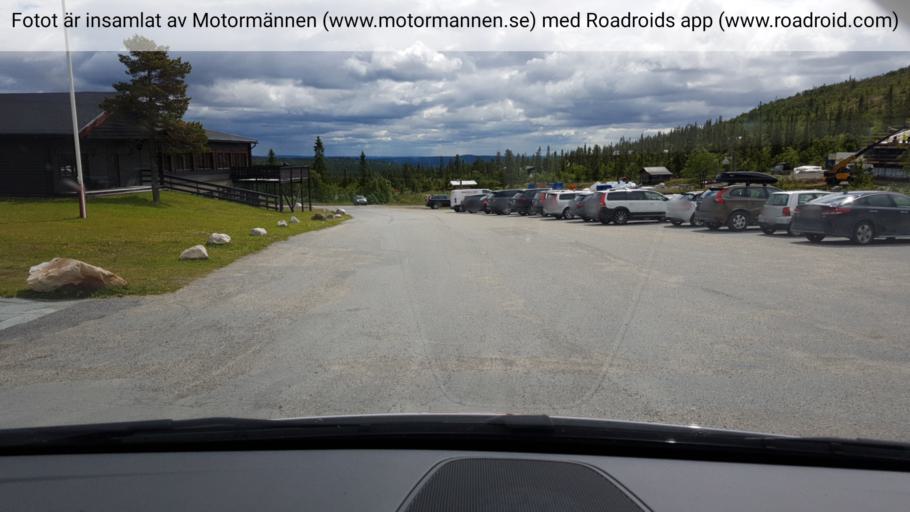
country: SE
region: Jaemtland
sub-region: Bergs Kommun
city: Hoverberg
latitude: 62.5047
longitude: 14.0970
